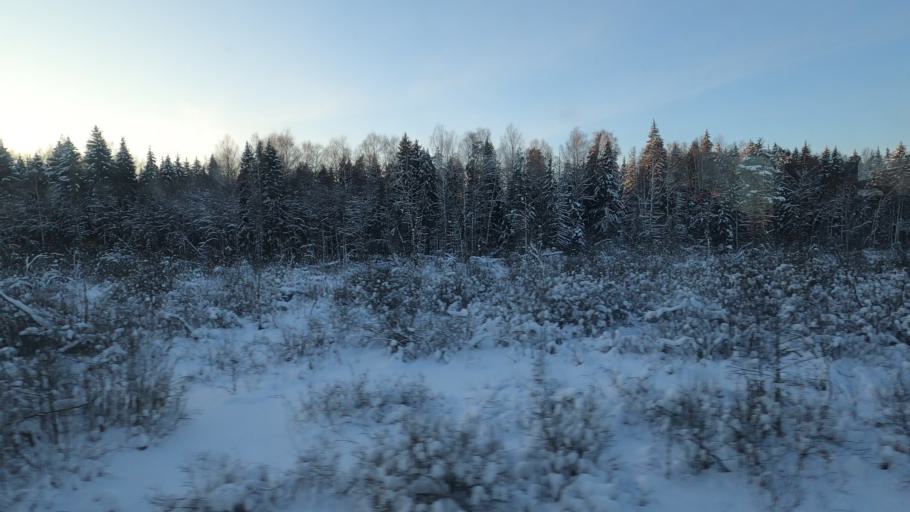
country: RU
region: Moskovskaya
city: Novo-Nikol'skoye
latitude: 56.5597
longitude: 37.5656
